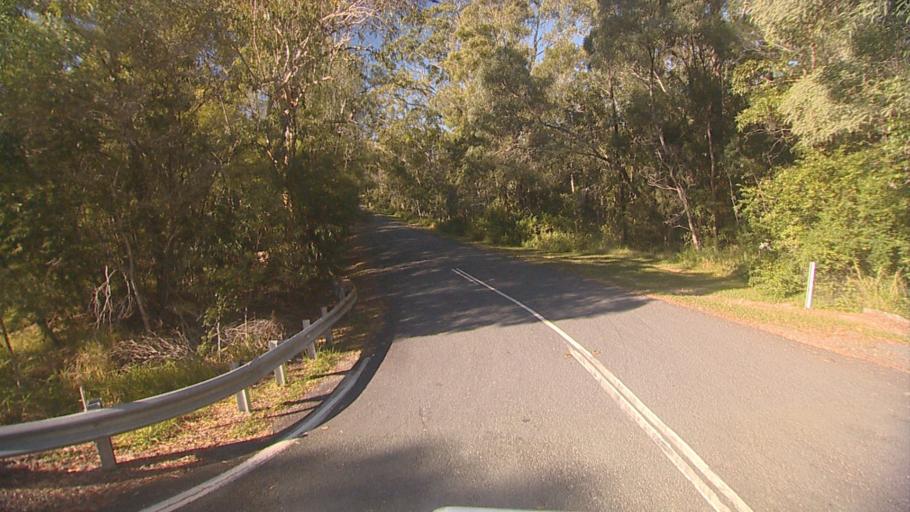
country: AU
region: Queensland
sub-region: Gold Coast
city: Yatala
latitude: -27.6883
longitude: 153.2780
